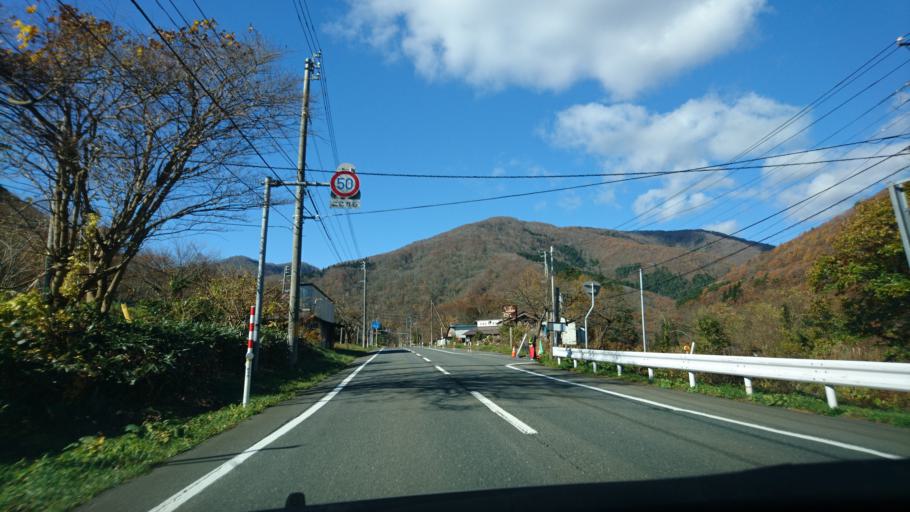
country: JP
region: Iwate
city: Kitakami
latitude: 39.3090
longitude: 140.9121
